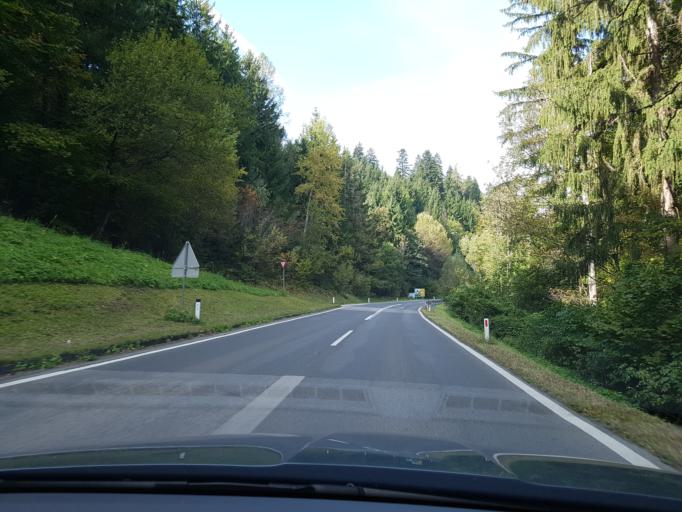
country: AT
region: Carinthia
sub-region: Politischer Bezirk Feldkirchen
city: Himmelberg
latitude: 46.7412
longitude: 14.0456
